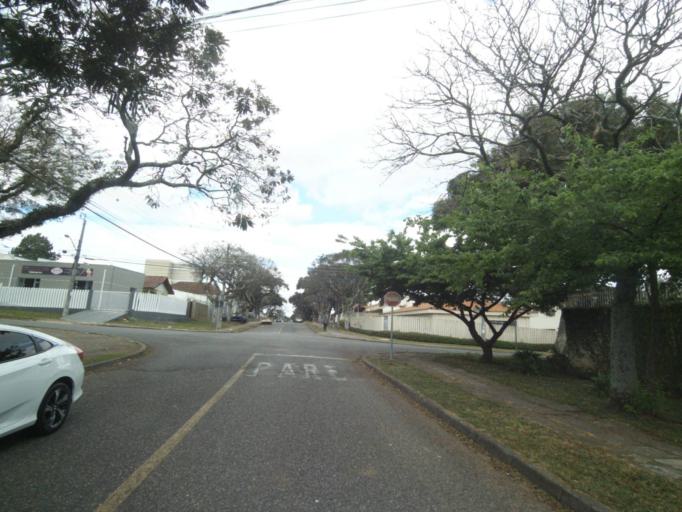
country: BR
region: Parana
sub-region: Curitiba
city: Curitiba
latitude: -25.4574
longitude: -49.2772
